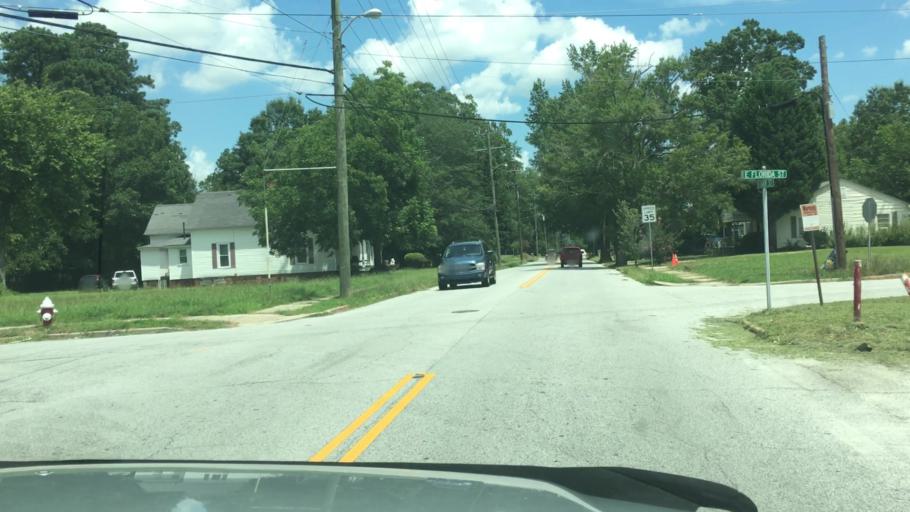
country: US
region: South Carolina
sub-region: Laurens County
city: Clinton
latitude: 34.4731
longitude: -81.8730
